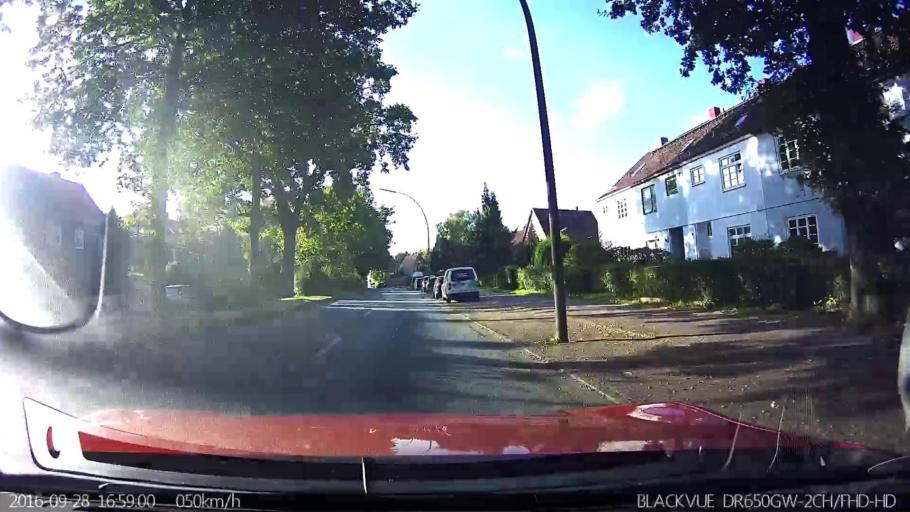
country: DE
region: Hamburg
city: Eidelstedt
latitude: 53.5671
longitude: 9.8923
